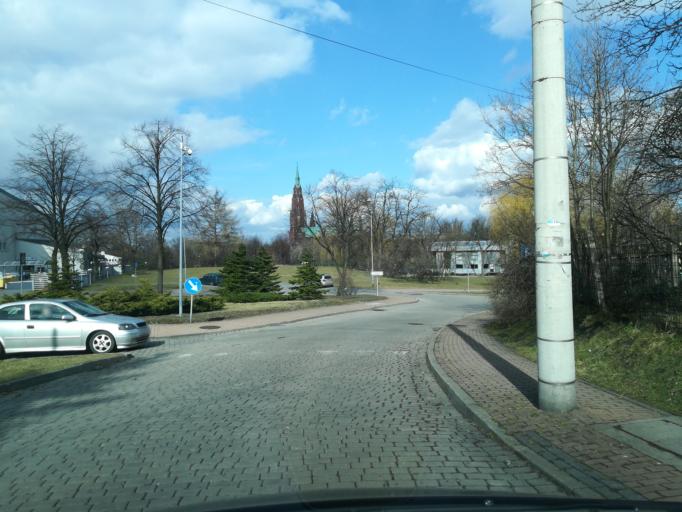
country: PL
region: Silesian Voivodeship
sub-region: Dabrowa Gornicza
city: Dabrowa Gornicza
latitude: 50.3195
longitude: 19.1913
